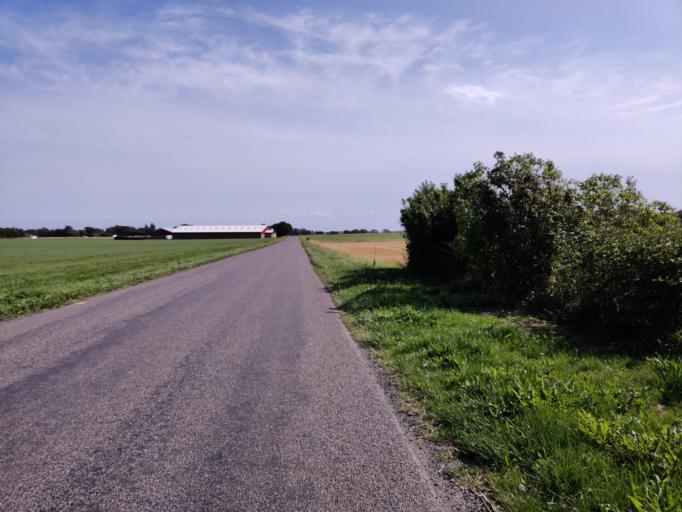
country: DK
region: Zealand
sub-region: Guldborgsund Kommune
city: Nykobing Falster
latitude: 54.6074
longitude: 11.9263
